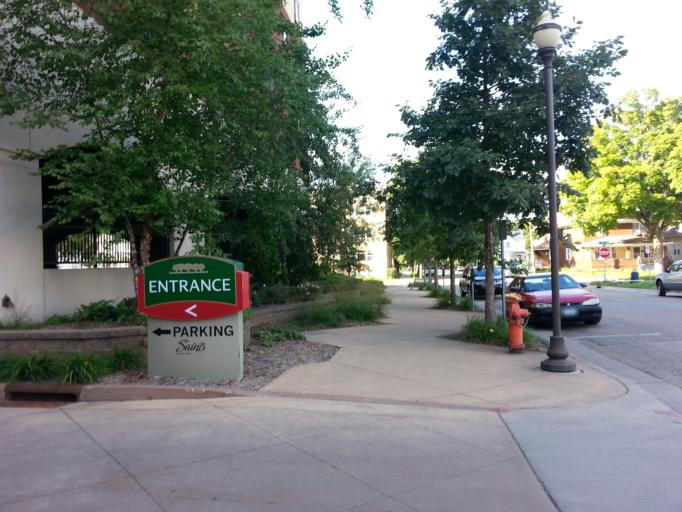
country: US
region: Minnesota
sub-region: Olmsted County
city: Rochester
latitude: 44.0221
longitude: -92.4835
